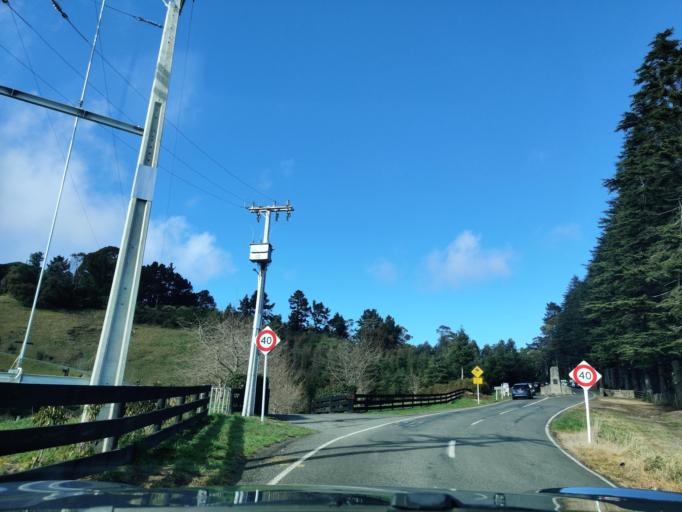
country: NZ
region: Hawke's Bay
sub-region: Hastings District
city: Hastings
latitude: -39.6937
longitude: 176.9022
